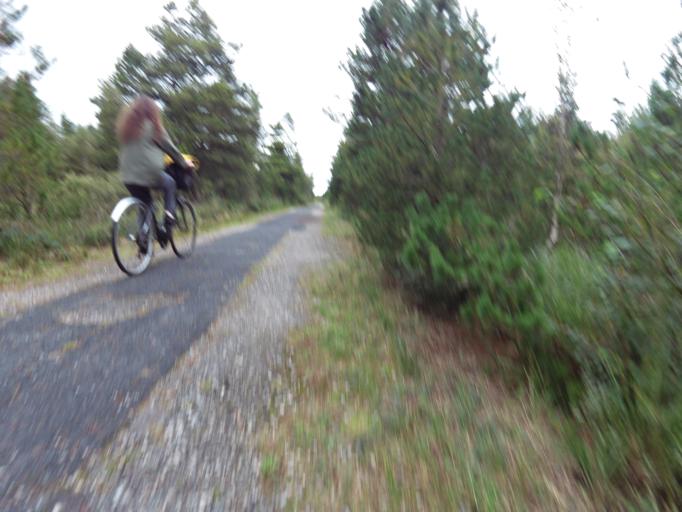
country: IE
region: Leinster
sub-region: Uibh Fhaili
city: Ferbane
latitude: 53.2171
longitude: -7.7518
